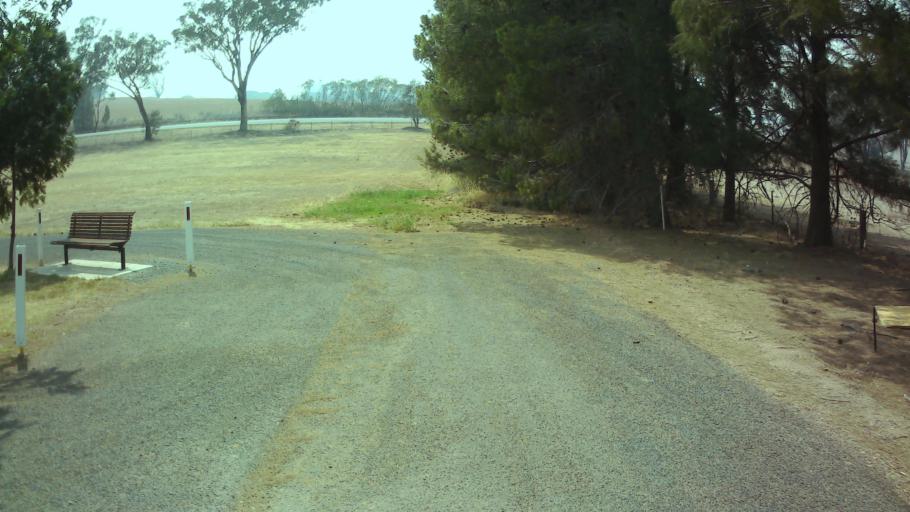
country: AU
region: New South Wales
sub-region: Weddin
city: Grenfell
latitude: -33.9199
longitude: 148.1584
